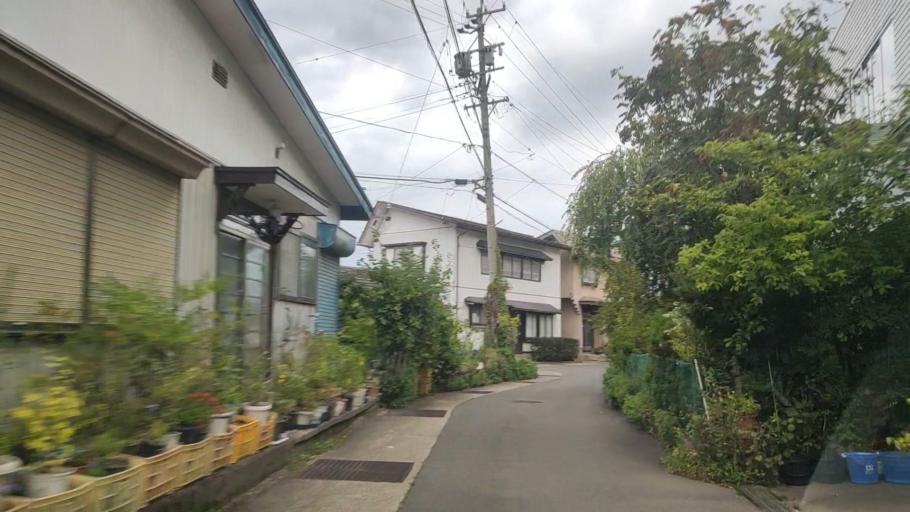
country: JP
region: Nagano
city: Nakano
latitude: 36.7835
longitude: 138.3677
